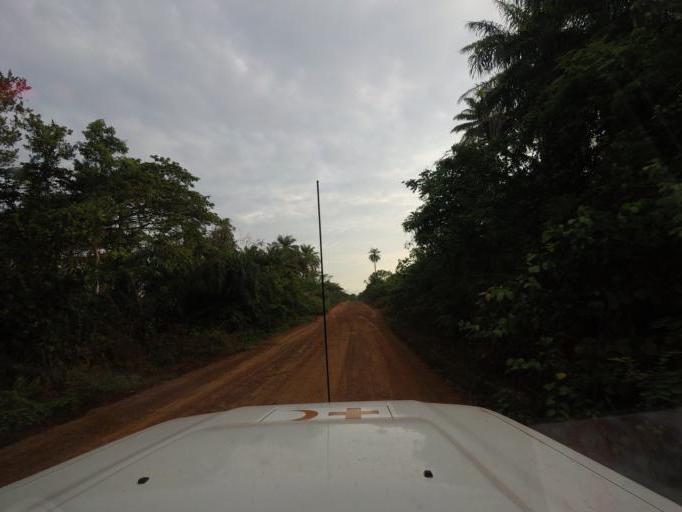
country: GN
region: Nzerekore
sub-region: Yomou
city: Yomou
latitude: 7.6372
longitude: -9.4713
